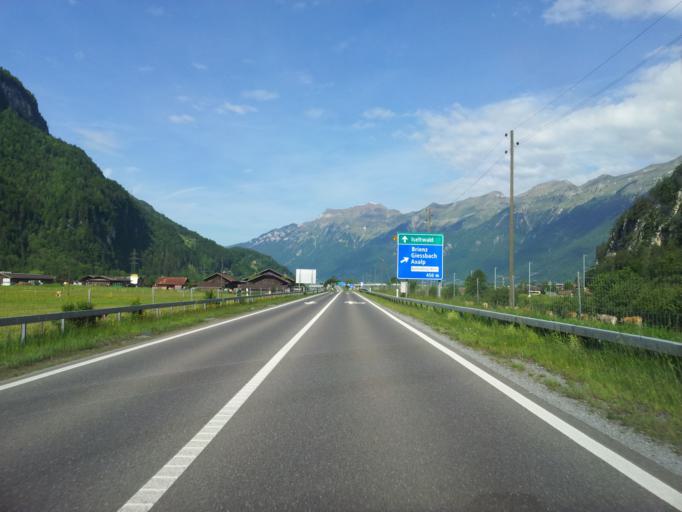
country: CH
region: Bern
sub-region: Interlaken-Oberhasli District
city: Brienz
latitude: 46.7429
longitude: 8.0709
